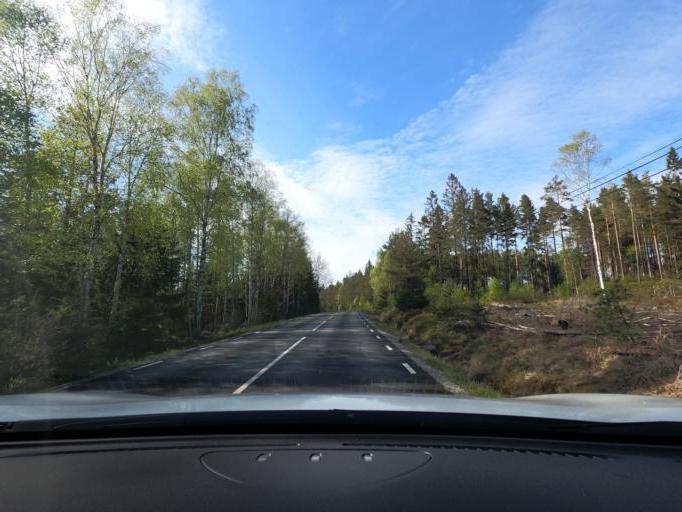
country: SE
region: Vaestra Goetaland
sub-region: Harryda Kommun
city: Landvetter
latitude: 57.6373
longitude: 12.2586
